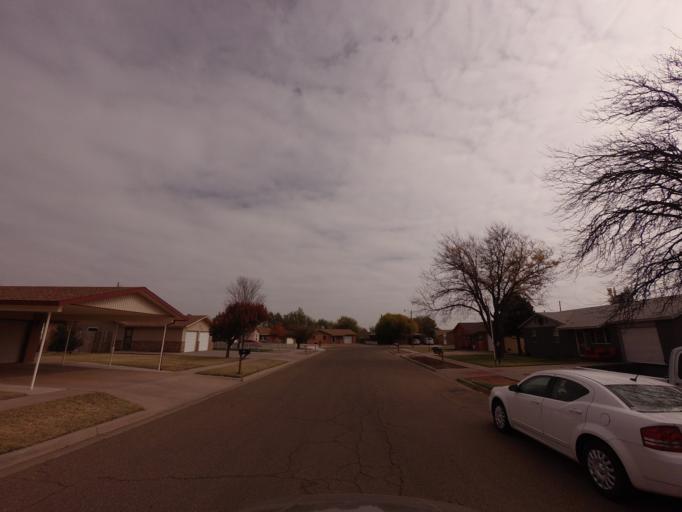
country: US
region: New Mexico
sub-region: Curry County
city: Clovis
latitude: 34.4291
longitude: -103.2300
